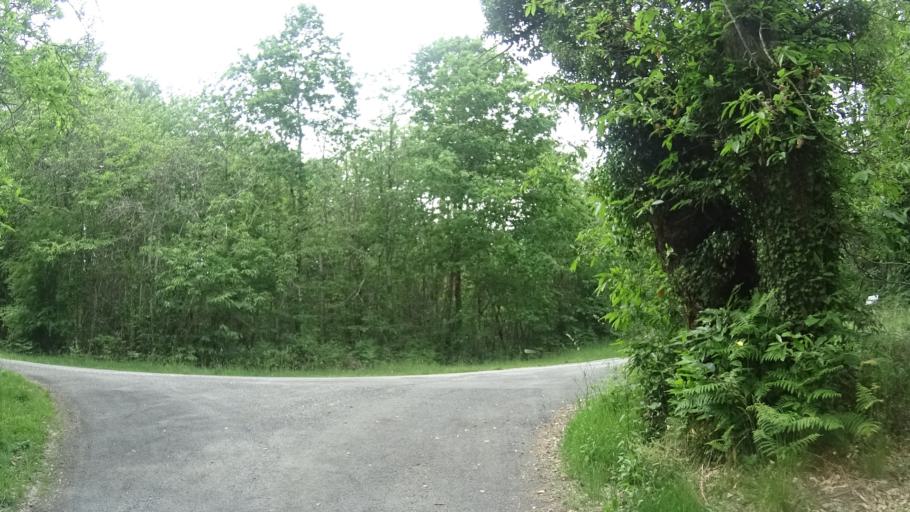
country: FR
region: Aquitaine
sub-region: Departement de la Dordogne
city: Lembras
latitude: 44.9734
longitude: 0.5039
